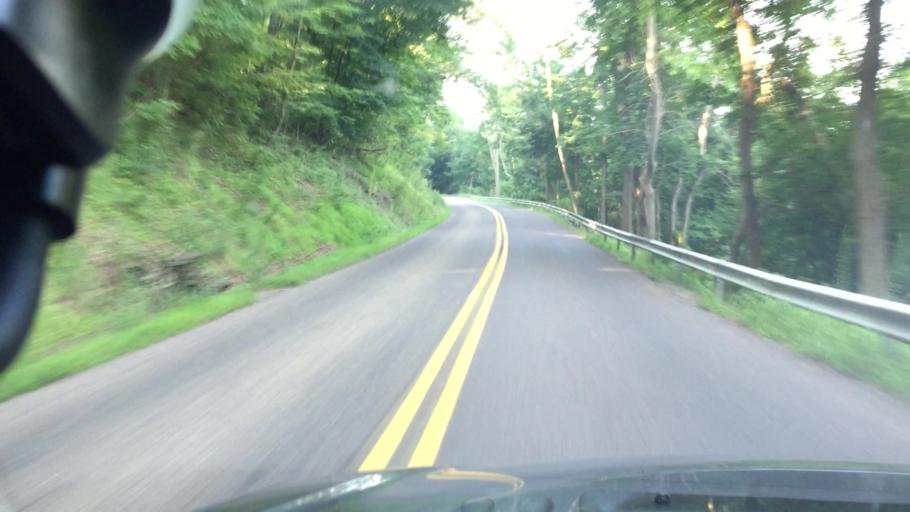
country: US
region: Pennsylvania
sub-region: Columbia County
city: Catawissa
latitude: 40.9531
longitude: -76.4492
